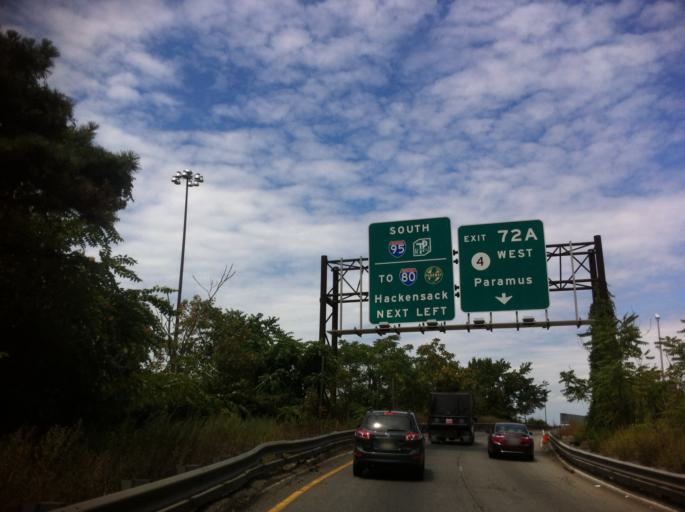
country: US
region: New Jersey
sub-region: Bergen County
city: Fort Lee
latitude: 40.8591
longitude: -73.9748
